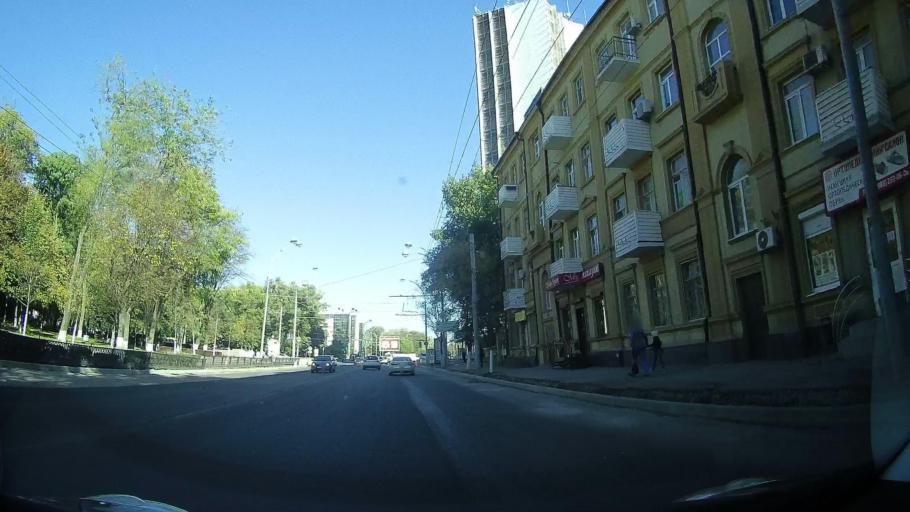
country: RU
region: Rostov
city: Rostov-na-Donu
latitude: 47.2271
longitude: 39.7416
